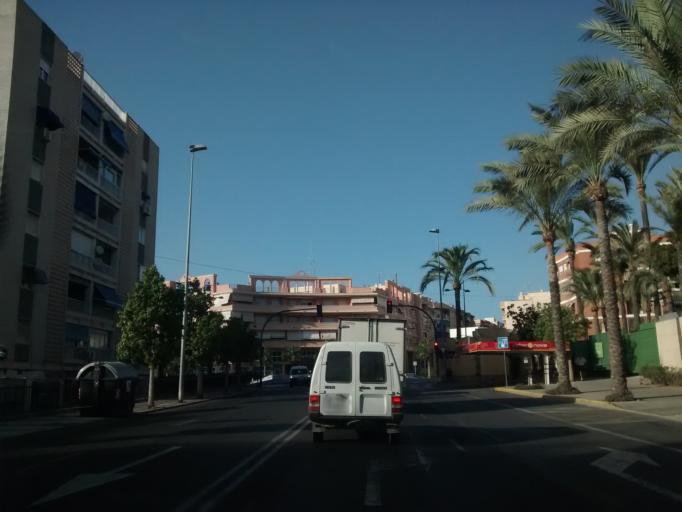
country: ES
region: Valencia
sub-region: Provincia de Alicante
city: Santa Pola
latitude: 38.1955
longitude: -0.5602
